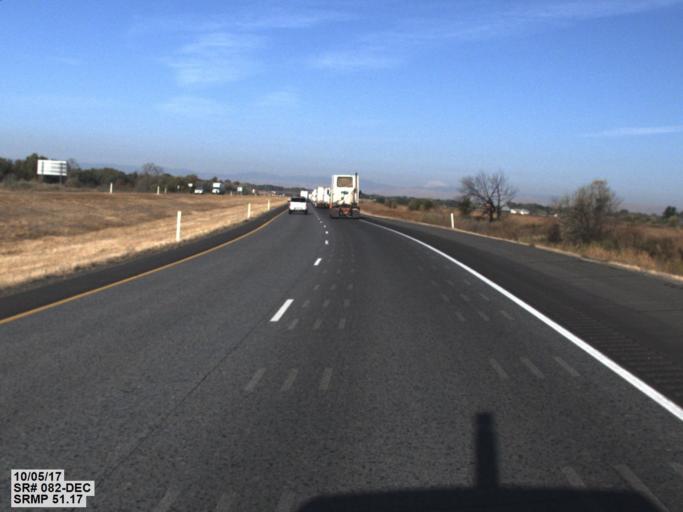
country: US
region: Washington
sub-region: Yakima County
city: Zillah
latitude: 46.4120
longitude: -120.2928
